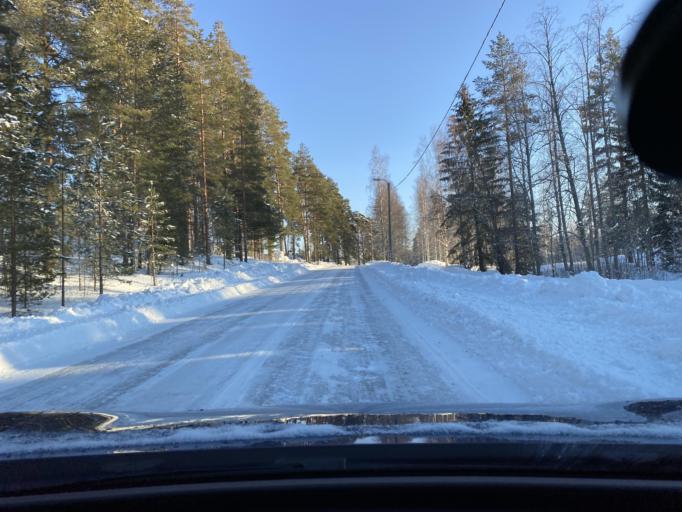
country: FI
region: Southern Savonia
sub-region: Mikkeli
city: Kangasniemi
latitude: 62.0008
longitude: 26.6263
